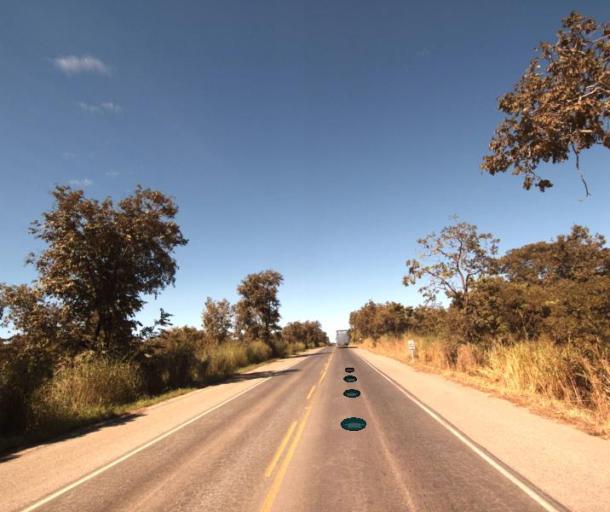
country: BR
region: Goias
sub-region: Itapaci
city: Itapaci
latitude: -14.9481
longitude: -49.3758
